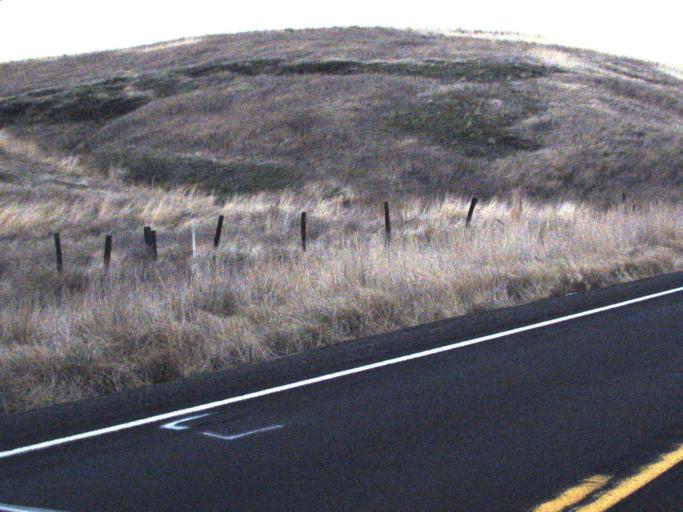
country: US
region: Washington
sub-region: Columbia County
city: Dayton
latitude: 46.4506
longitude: -117.9586
